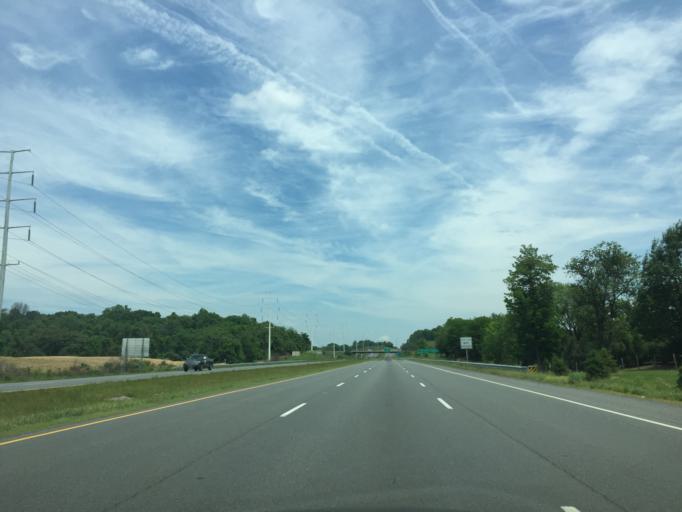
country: US
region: Virginia
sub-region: City of Winchester
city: Winchester
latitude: 39.1967
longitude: -78.1944
